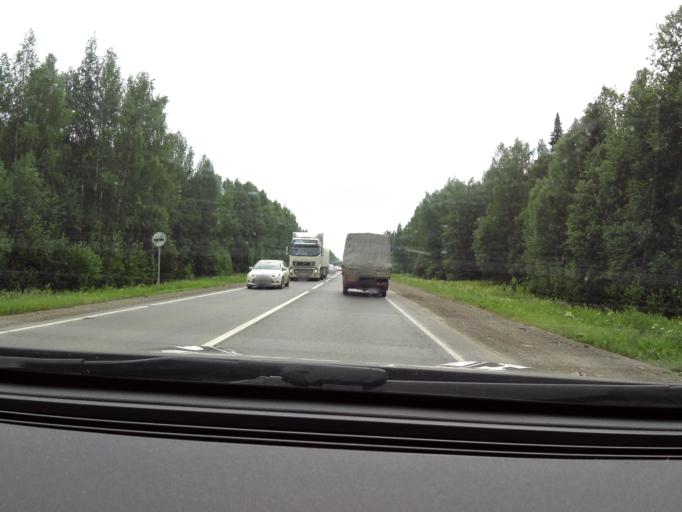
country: RU
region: Perm
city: Kukushtan
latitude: 57.5777
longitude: 56.5575
